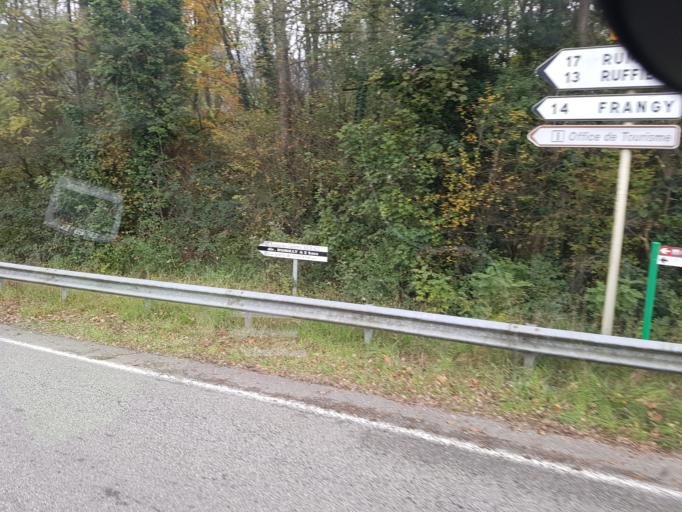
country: FR
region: Rhone-Alpes
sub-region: Departement de la Haute-Savoie
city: Versonnex
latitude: 45.9520
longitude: 5.8326
